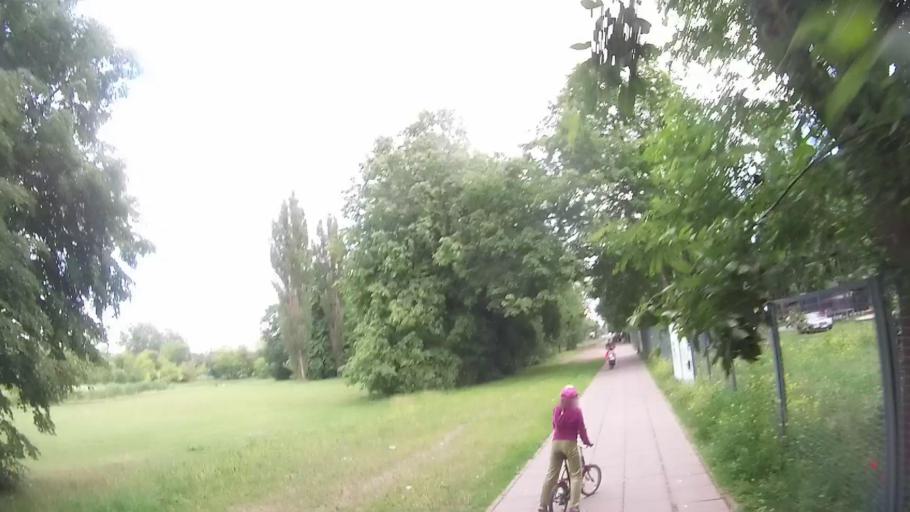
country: PL
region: Masovian Voivodeship
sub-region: Warszawa
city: Praga Poludnie
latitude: 52.2435
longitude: 21.0606
